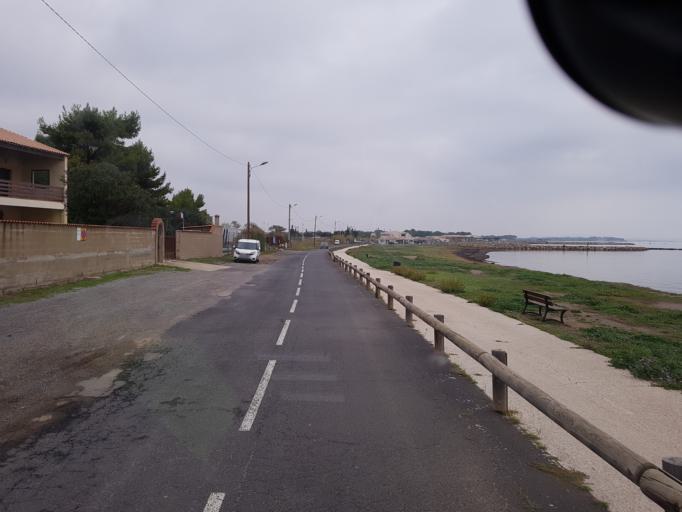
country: FR
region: Languedoc-Roussillon
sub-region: Departement de l'Herault
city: Marseillan
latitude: 43.3592
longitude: 3.5353
